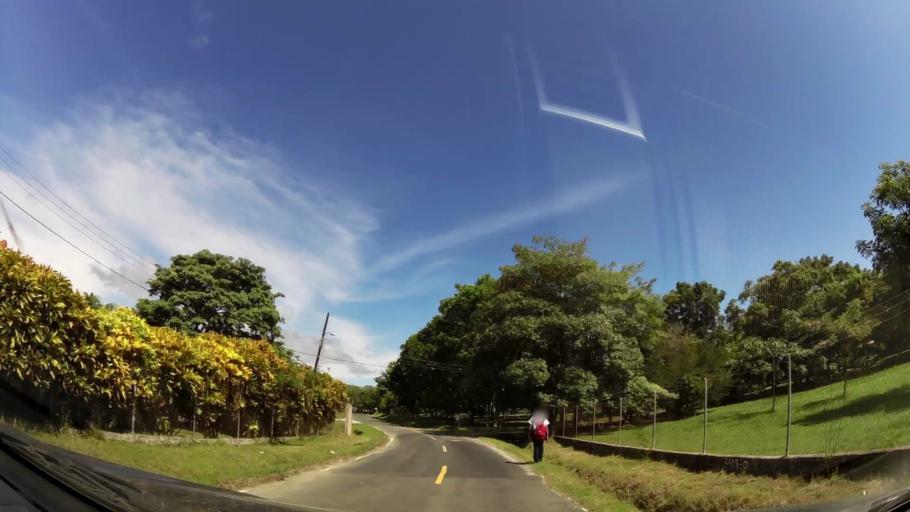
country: PA
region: Panama
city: Nueva Gorgona
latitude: 8.5589
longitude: -79.8682
